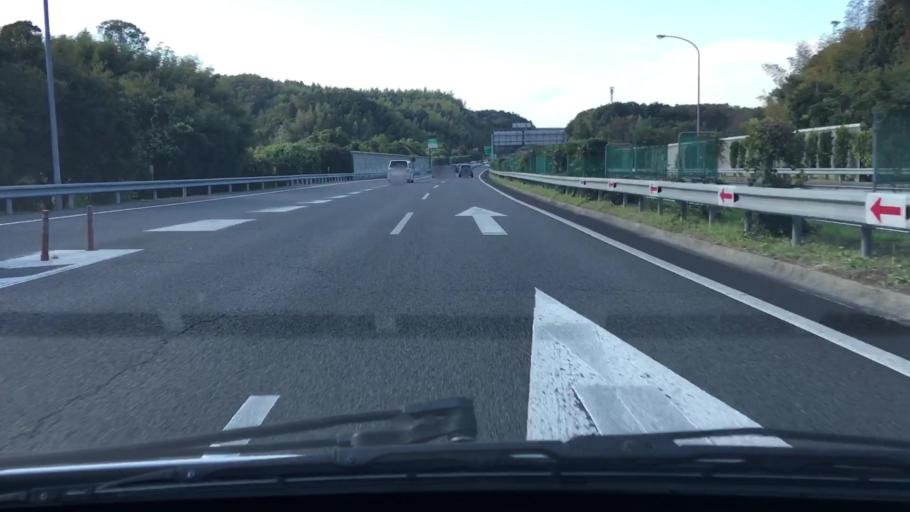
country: JP
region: Chiba
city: Kisarazu
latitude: 35.3724
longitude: 139.9748
